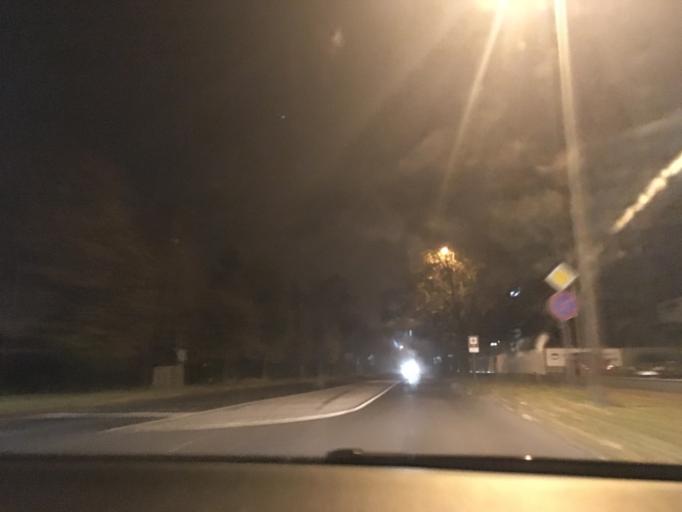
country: HU
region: Hajdu-Bihar
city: Debrecen
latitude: 47.5151
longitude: 21.6068
